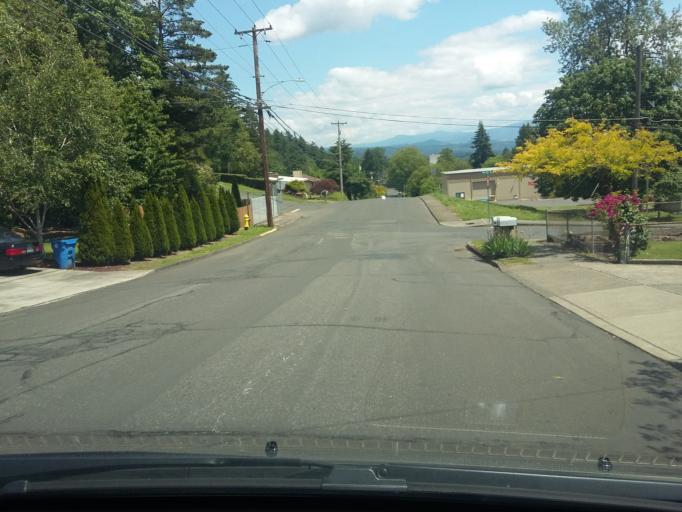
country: US
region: Washington
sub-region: Clark County
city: Camas
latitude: 45.5870
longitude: -122.4205
